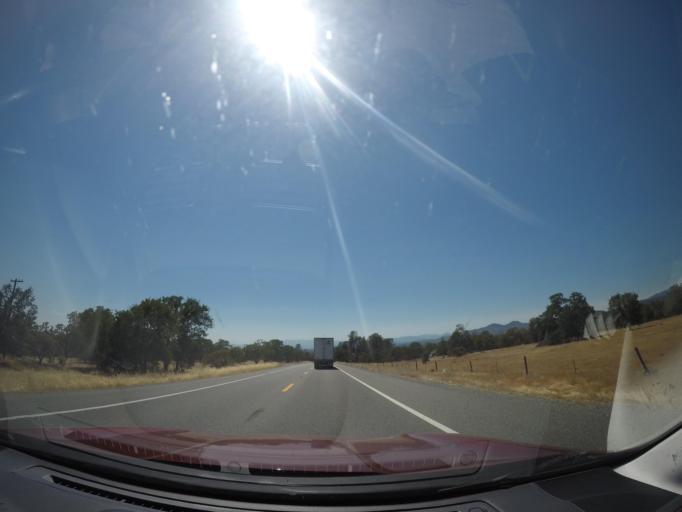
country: US
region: California
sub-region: Shasta County
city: Bella Vista
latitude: 40.6884
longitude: -122.1280
